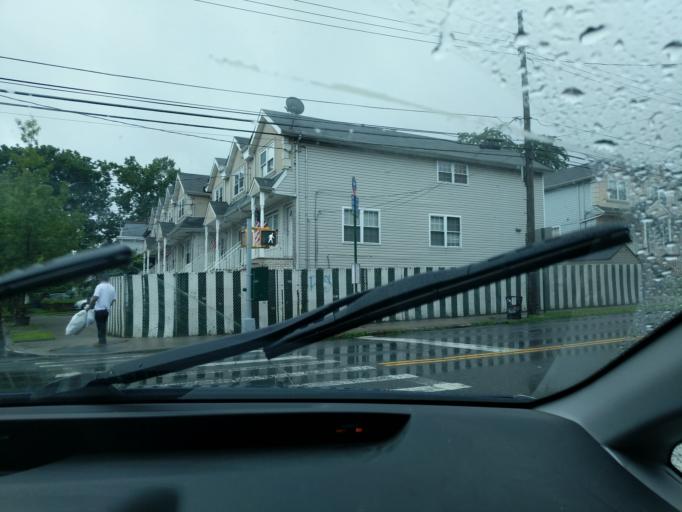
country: US
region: New Jersey
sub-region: Hudson County
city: Bayonne
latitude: 40.6352
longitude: -74.1326
